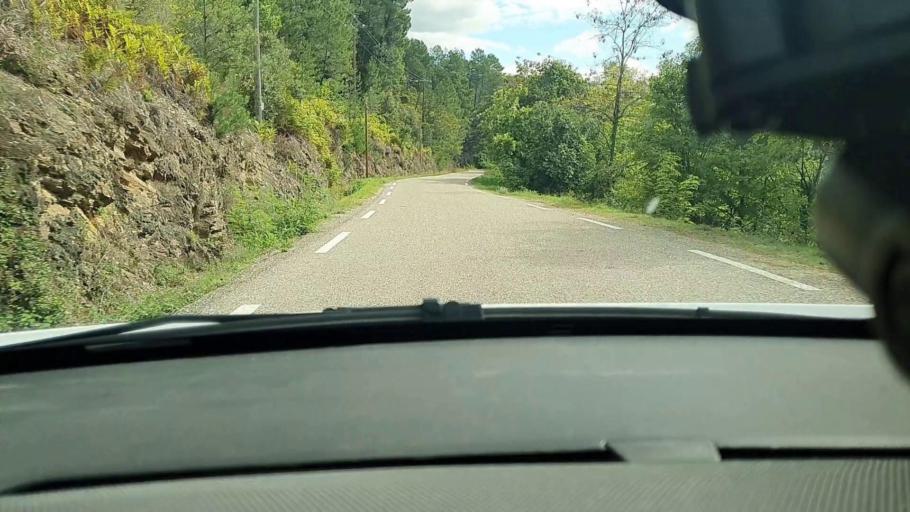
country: FR
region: Languedoc-Roussillon
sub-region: Departement du Gard
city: Branoux-les-Taillades
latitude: 44.3314
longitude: 3.9580
